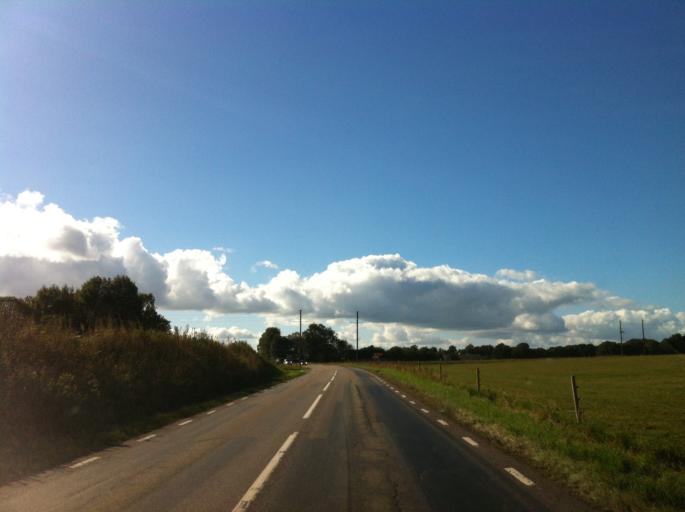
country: SE
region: Skane
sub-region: Sjobo Kommun
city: Sjoebo
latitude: 55.6379
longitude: 13.7595
